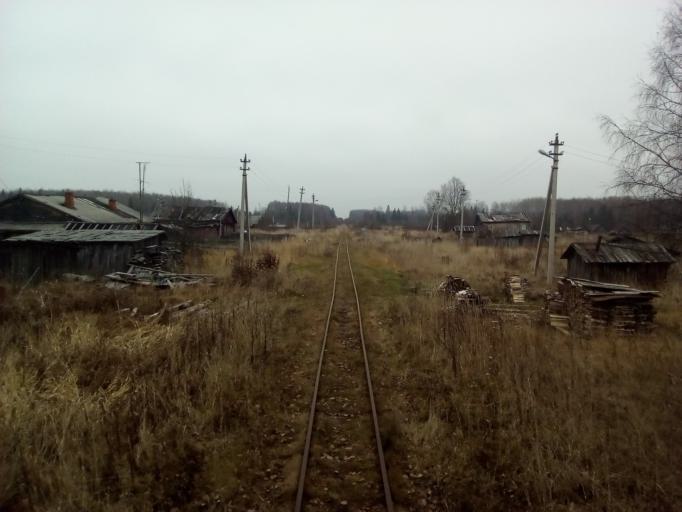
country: RU
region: Vologda
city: Kharovsk
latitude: 59.8029
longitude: 40.4587
